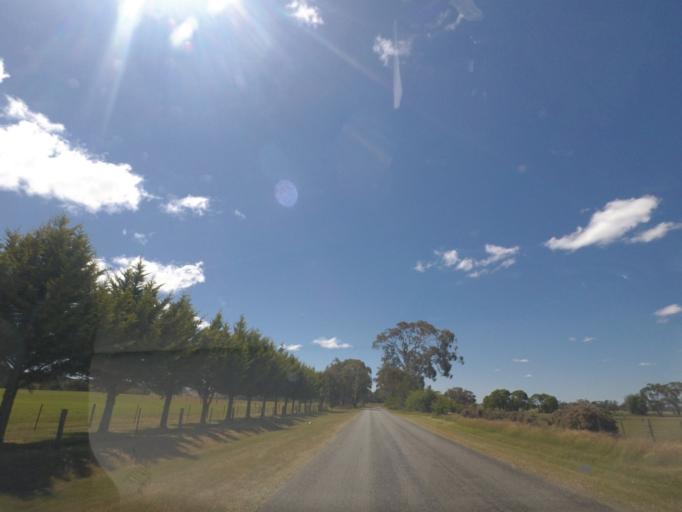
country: AU
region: Victoria
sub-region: Mount Alexander
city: Castlemaine
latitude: -37.3248
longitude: 144.4414
